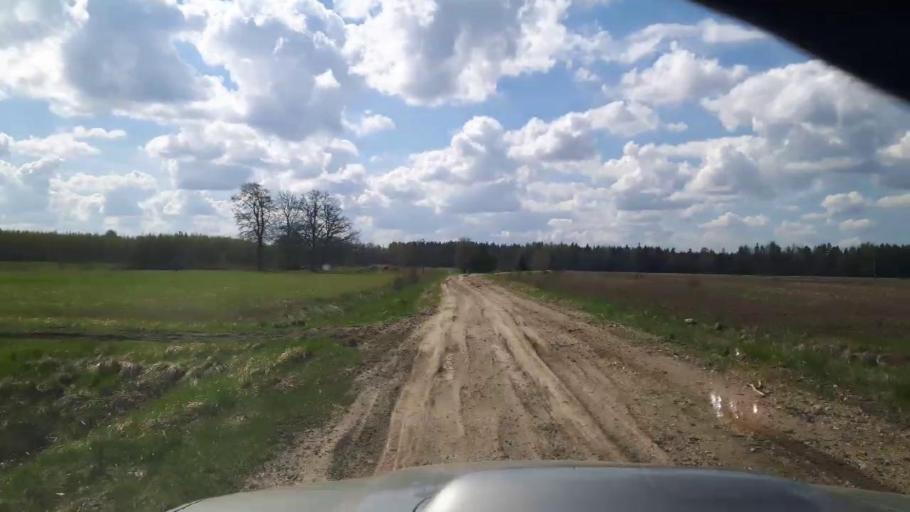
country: EE
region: Paernumaa
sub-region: Vaendra vald (alev)
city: Vandra
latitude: 58.5413
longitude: 25.0694
